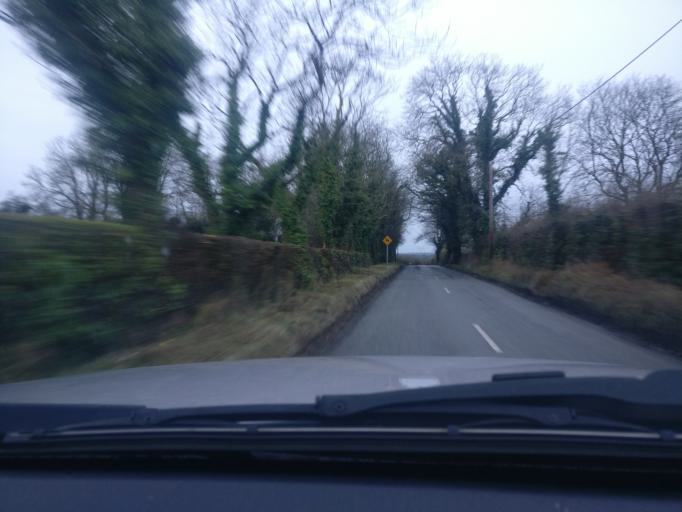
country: IE
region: Leinster
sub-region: Kildare
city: Kilcock
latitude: 53.4734
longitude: -6.6248
